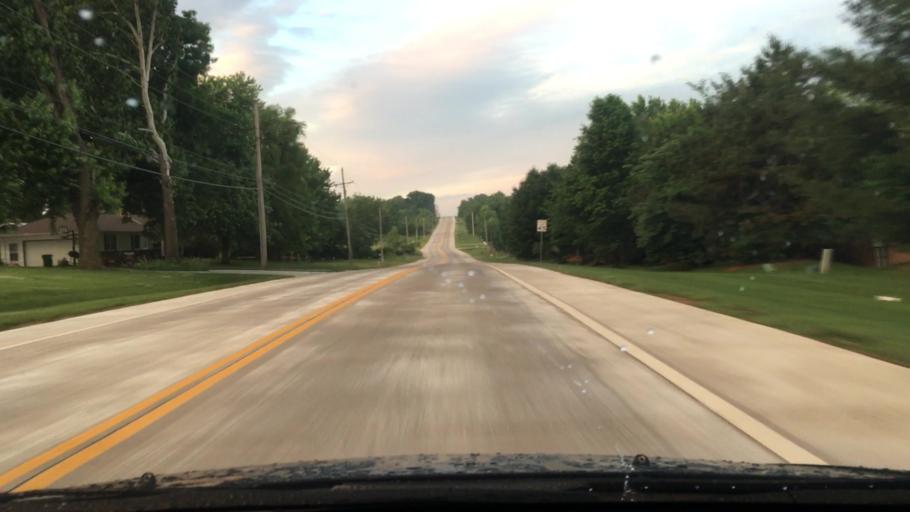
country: US
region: Missouri
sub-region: Jackson County
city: Lees Summit
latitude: 38.8629
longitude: -94.4167
